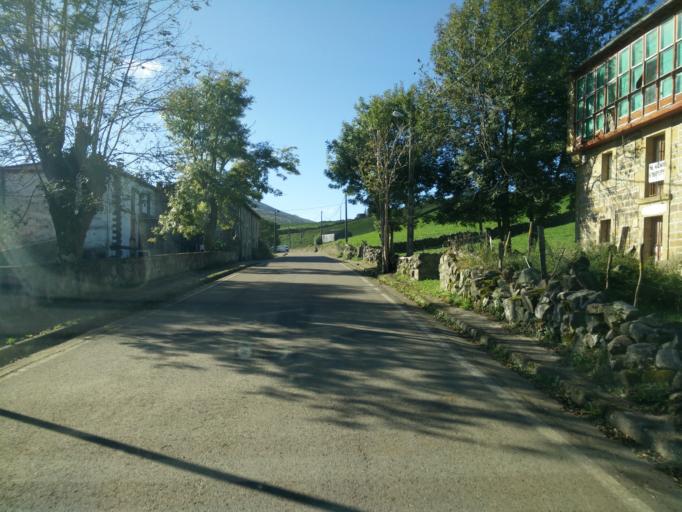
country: ES
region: Cantabria
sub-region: Provincia de Cantabria
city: San Pedro del Romeral
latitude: 43.1121
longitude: -3.8188
